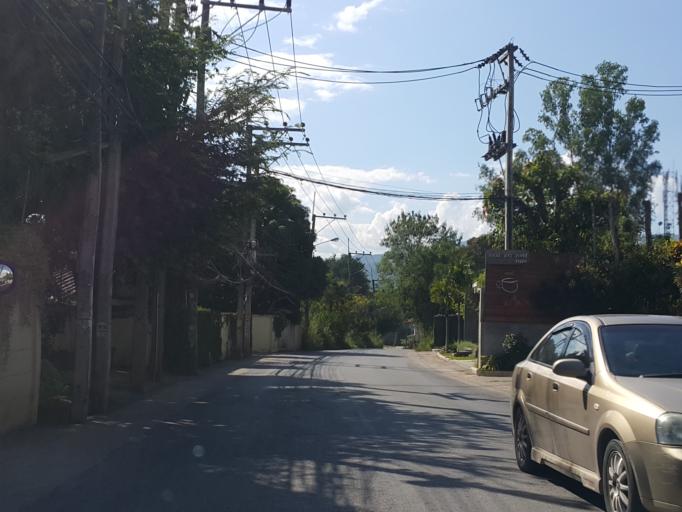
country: TH
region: Chiang Mai
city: San Sai
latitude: 18.9124
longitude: 98.9356
